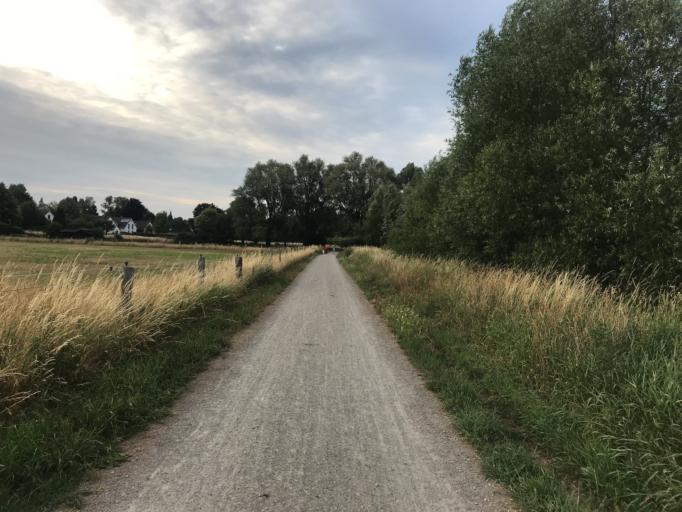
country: DE
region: Lower Saxony
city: Isernhagen Farster Bauerschaft
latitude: 52.4203
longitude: 9.8169
